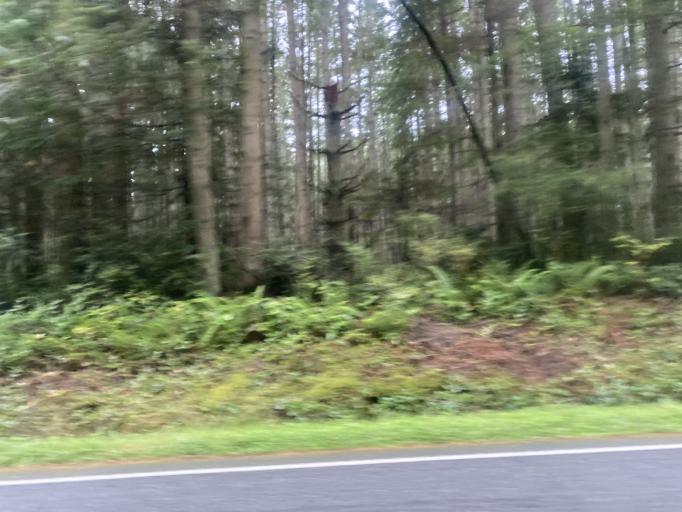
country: US
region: Washington
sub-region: Island County
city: Freeland
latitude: 48.0659
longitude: -122.4866
